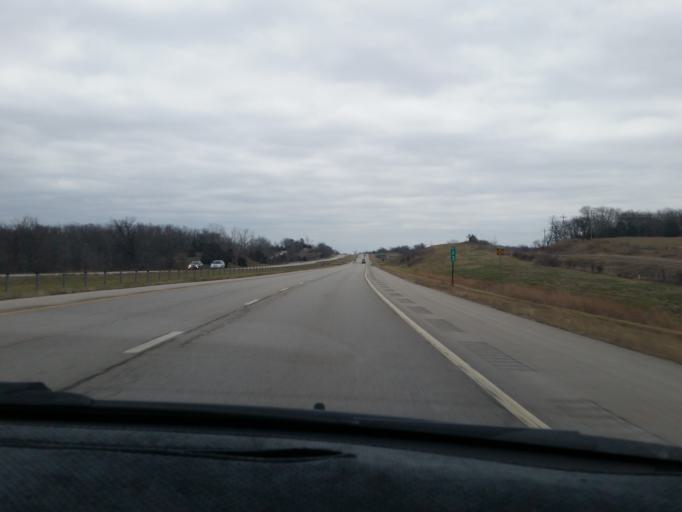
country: US
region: Kansas
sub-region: Douglas County
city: Eudora
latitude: 38.9429
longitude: -95.0667
